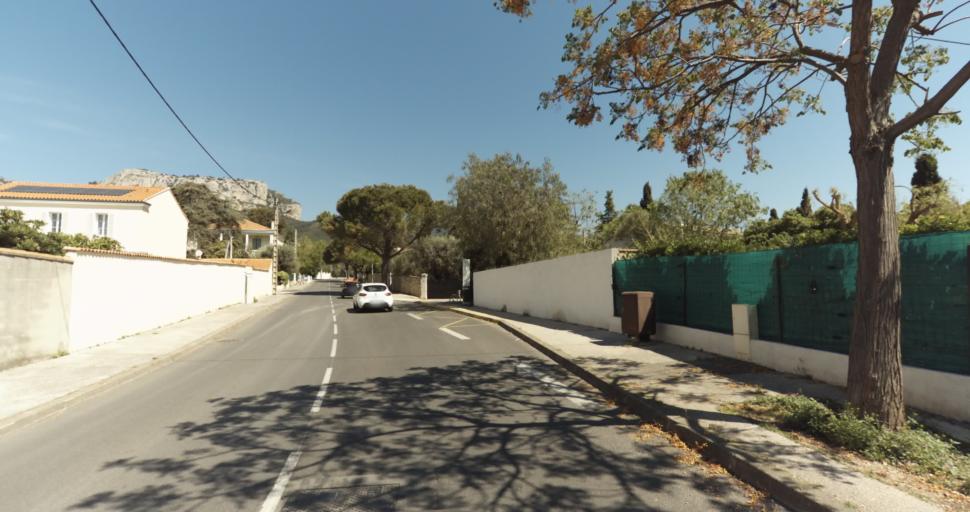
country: FR
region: Provence-Alpes-Cote d'Azur
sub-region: Departement du Var
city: Le Revest-les-Eaux
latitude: 43.1442
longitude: 5.9018
